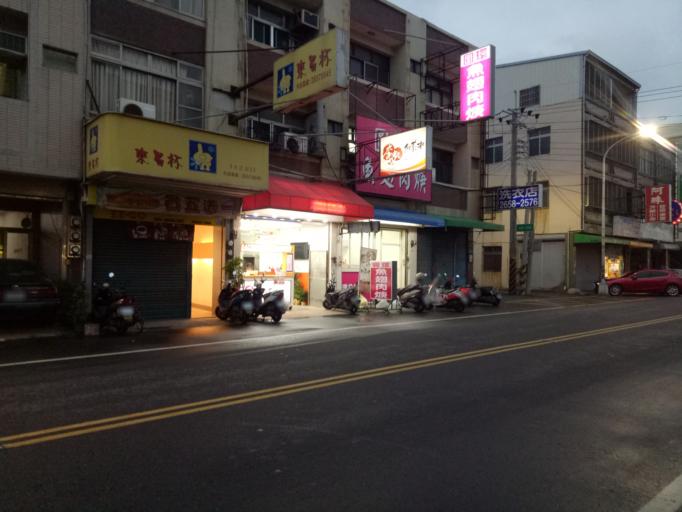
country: TW
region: Taiwan
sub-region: Changhua
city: Chang-hua
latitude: 24.2479
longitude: 120.5383
